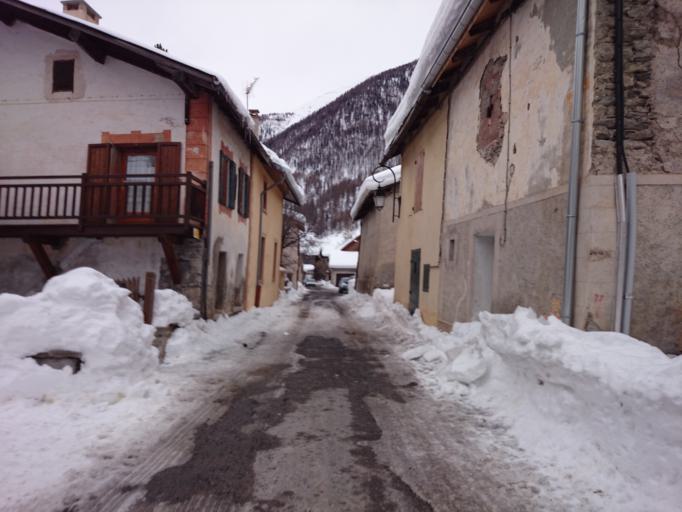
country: IT
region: Piedmont
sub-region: Provincia di Torino
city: Prali
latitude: 44.7938
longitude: 6.9282
